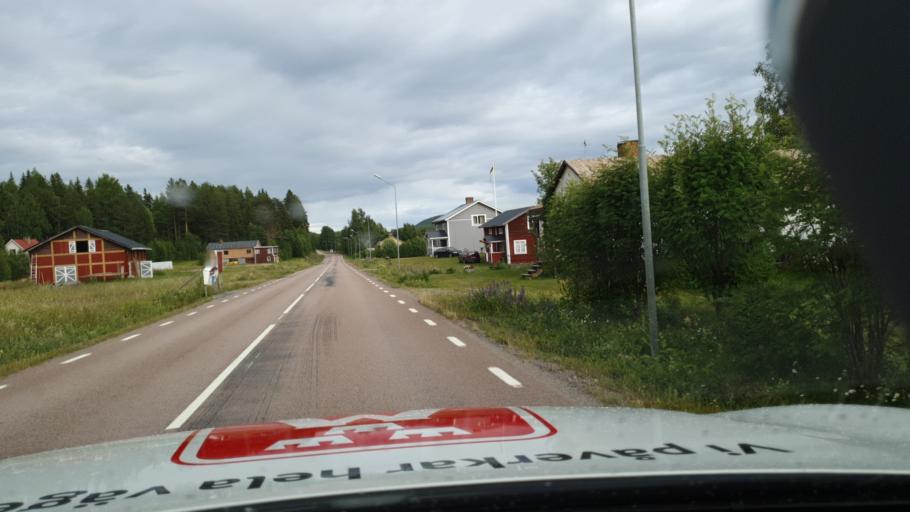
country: SE
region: Vaesternorrland
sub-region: Solleftea Kommun
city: As
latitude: 63.5951
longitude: 16.1702
